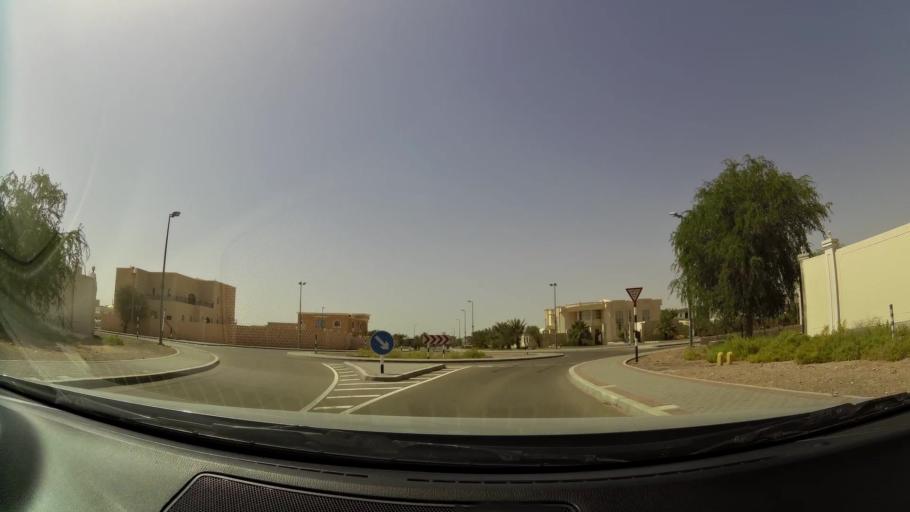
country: OM
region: Al Buraimi
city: Al Buraymi
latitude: 24.3112
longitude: 55.7527
